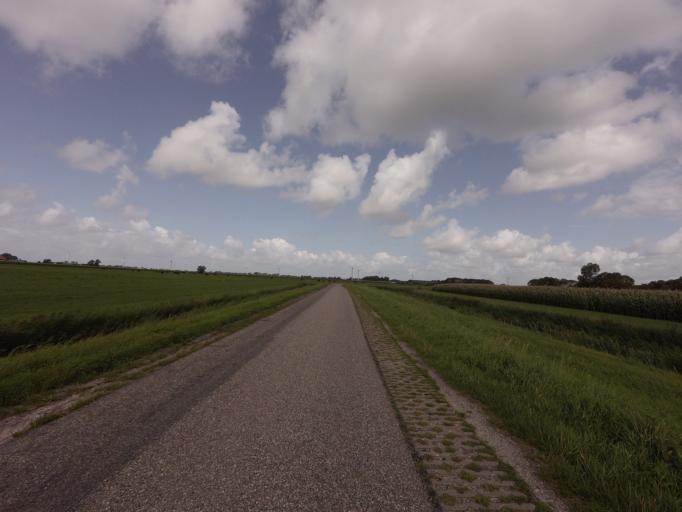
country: NL
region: Friesland
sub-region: Gemeente Franekeradeel
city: Sexbierum
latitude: 53.1688
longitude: 5.4859
